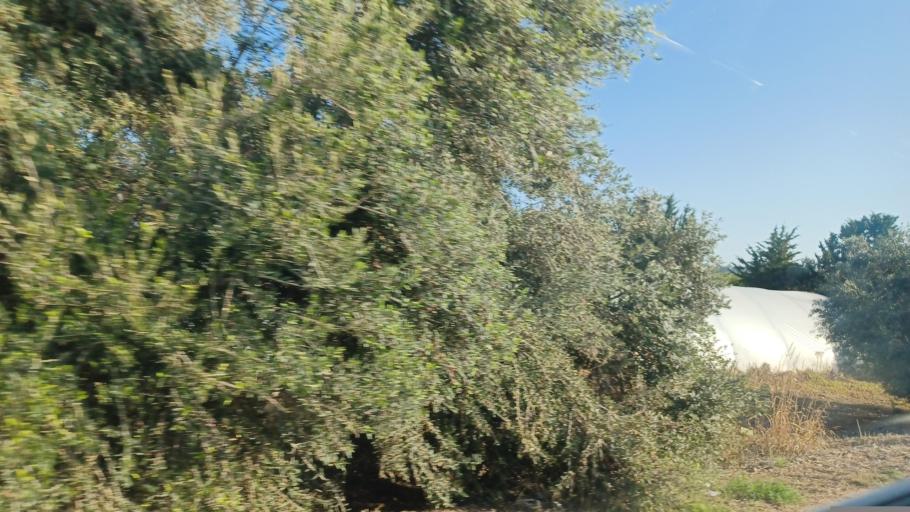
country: CY
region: Pafos
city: Paphos
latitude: 34.7192
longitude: 32.5272
